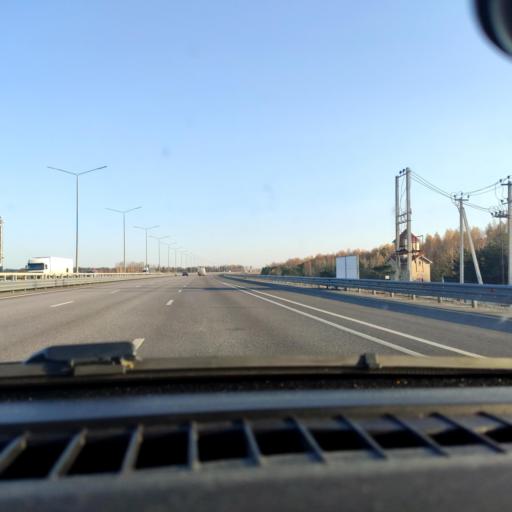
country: RU
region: Voronezj
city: Somovo
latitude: 51.7866
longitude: 39.2826
